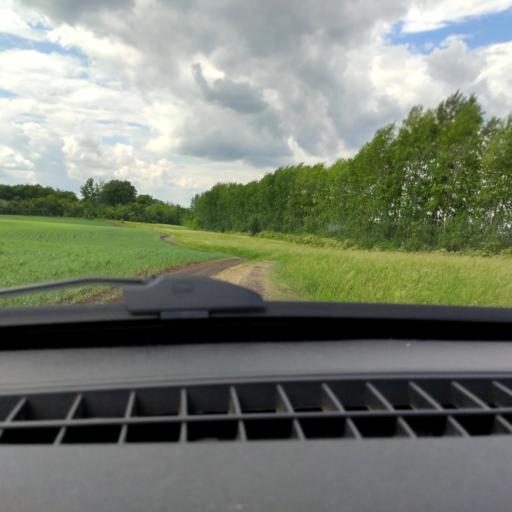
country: RU
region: Bashkortostan
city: Kabakovo
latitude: 54.5170
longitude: 56.0911
